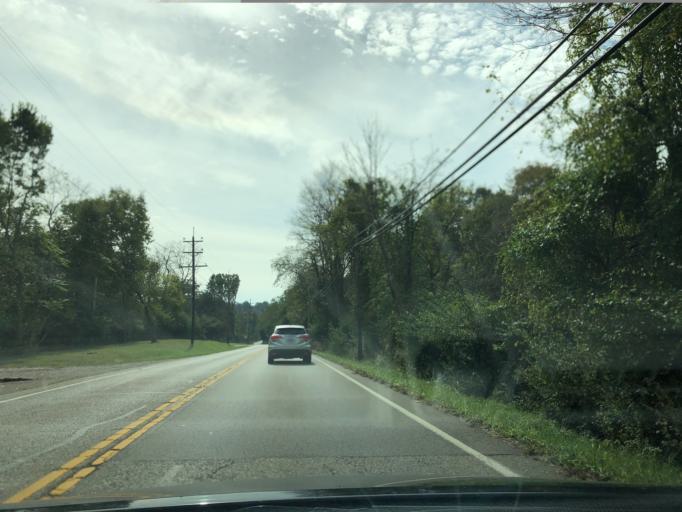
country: US
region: Ohio
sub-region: Clermont County
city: Milford
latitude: 39.1868
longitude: -84.2924
